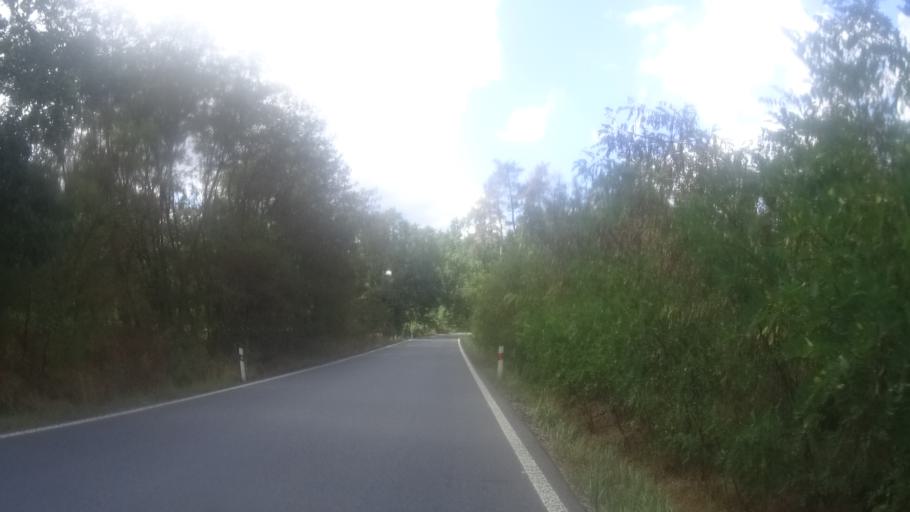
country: CZ
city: Borohradek
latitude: 50.0848
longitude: 16.1125
